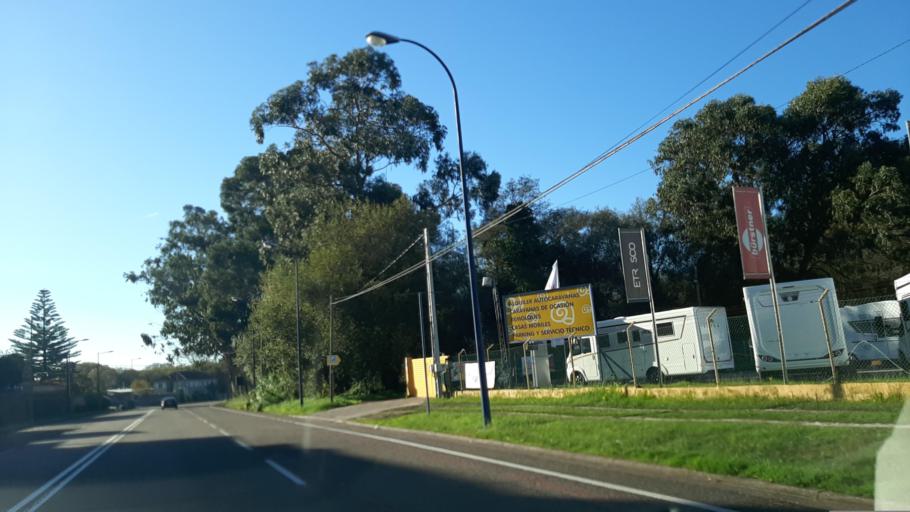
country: ES
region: Galicia
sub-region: Provincia de Pontevedra
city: Vigo
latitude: 42.2115
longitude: -8.7682
